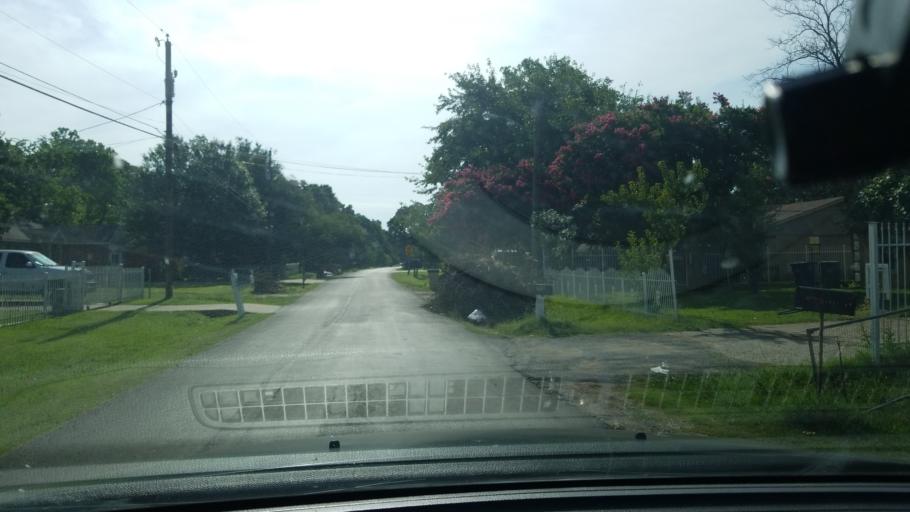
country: US
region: Texas
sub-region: Dallas County
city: Balch Springs
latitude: 32.7152
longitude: -96.6446
